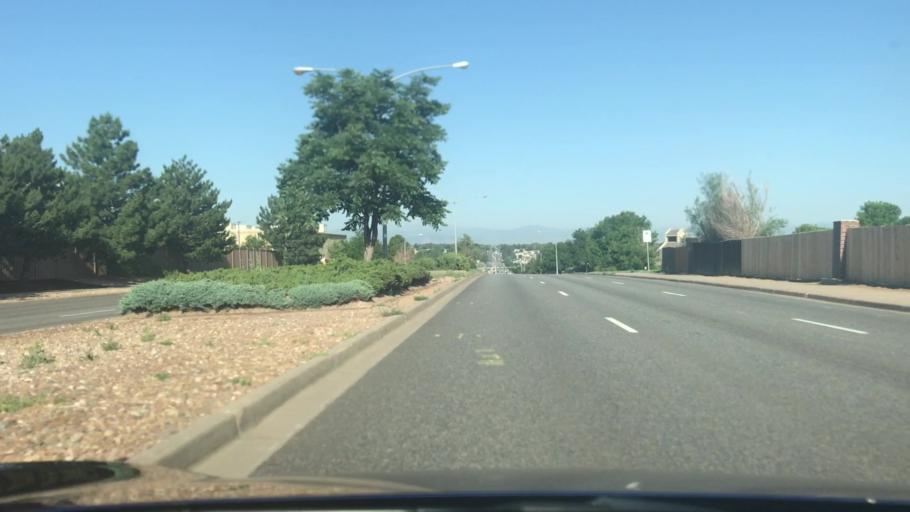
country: US
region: Colorado
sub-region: Arapahoe County
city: Dove Valley
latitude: 39.6531
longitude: -104.7650
